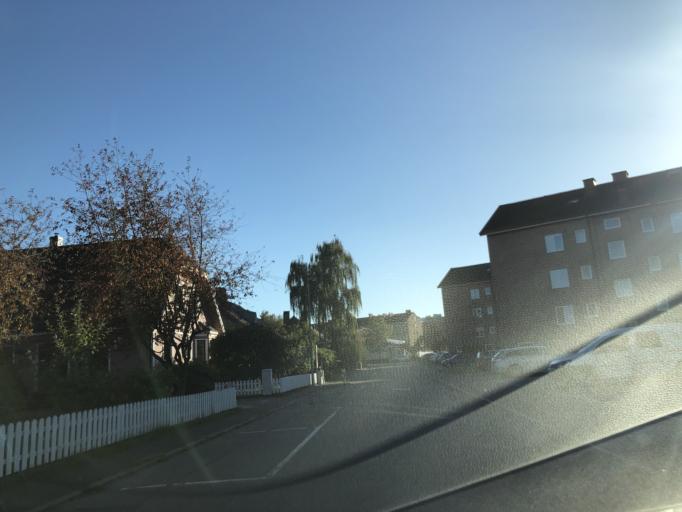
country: SE
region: Vaestra Goetaland
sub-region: Molndal
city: Moelndal
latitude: 57.6627
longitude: 12.0075
